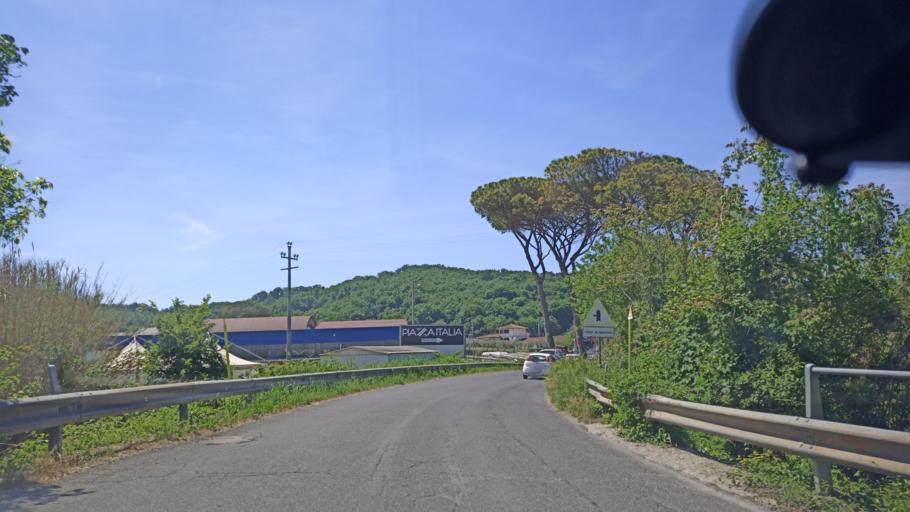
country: IT
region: Latium
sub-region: Provincia di Rieti
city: Stimigliano
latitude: 42.3136
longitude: 12.5760
